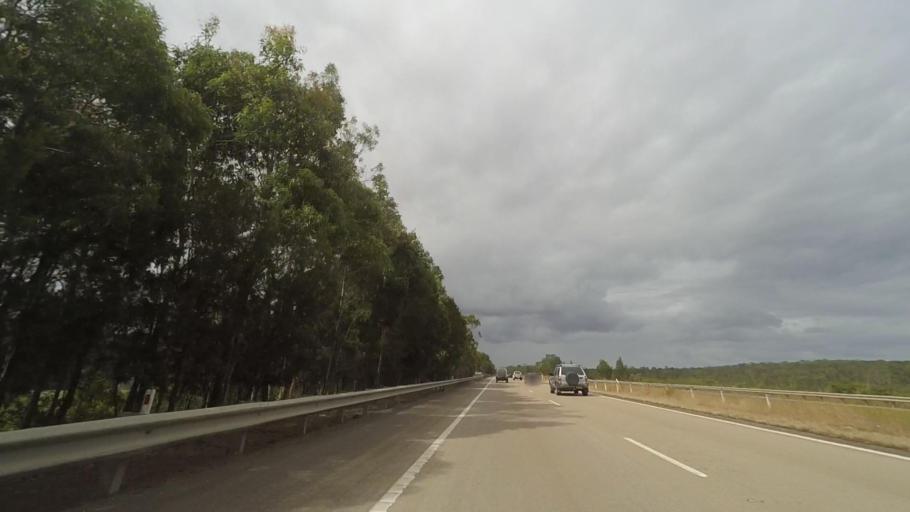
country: AU
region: New South Wales
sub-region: Port Stephens Shire
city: Raymond Terrace
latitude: -32.7326
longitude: 151.7819
